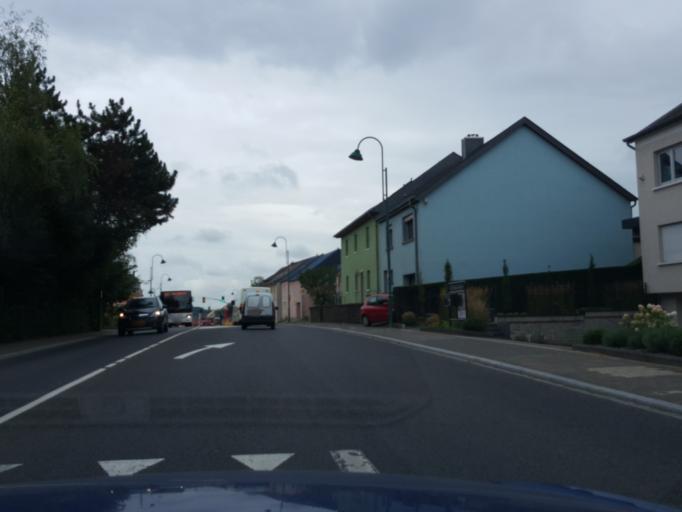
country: LU
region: Luxembourg
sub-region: Canton de Capellen
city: Mamer
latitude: 49.6330
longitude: 6.0189
